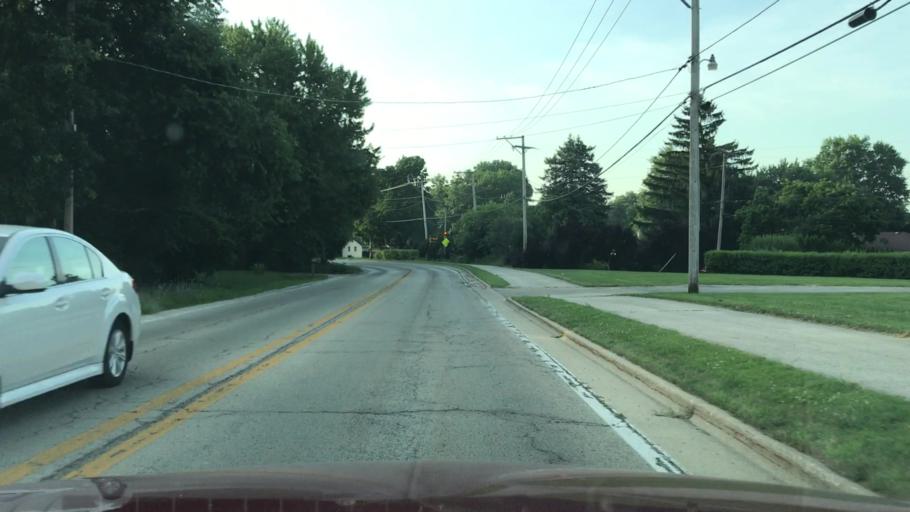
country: US
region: Illinois
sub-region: Winnebago County
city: Rockford
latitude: 42.2486
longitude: -89.0245
